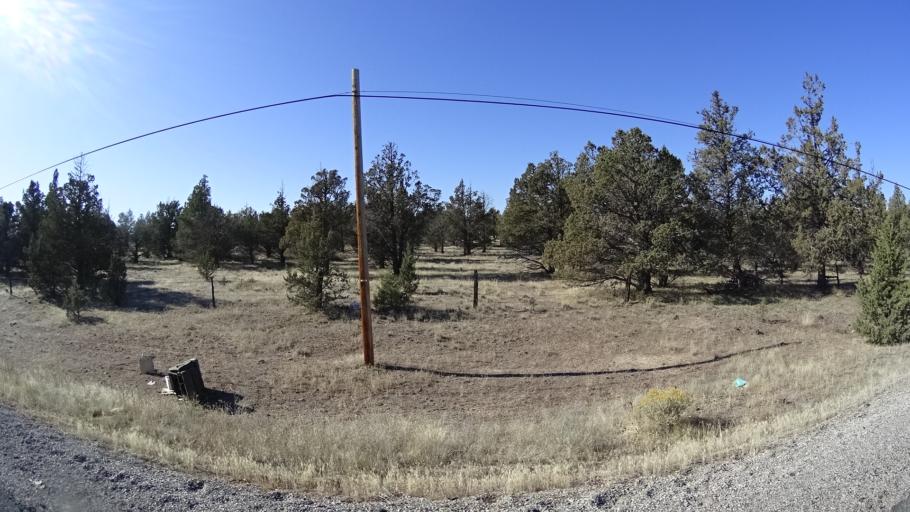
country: US
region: California
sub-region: Siskiyou County
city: Montague
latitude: 41.6584
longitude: -122.3657
